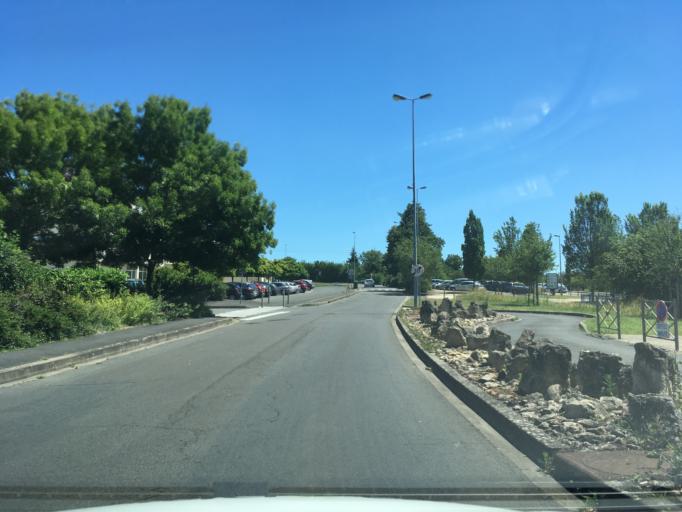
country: FR
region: Poitou-Charentes
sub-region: Departement des Deux-Sevres
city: Niort
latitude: 46.3397
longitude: -0.4369
